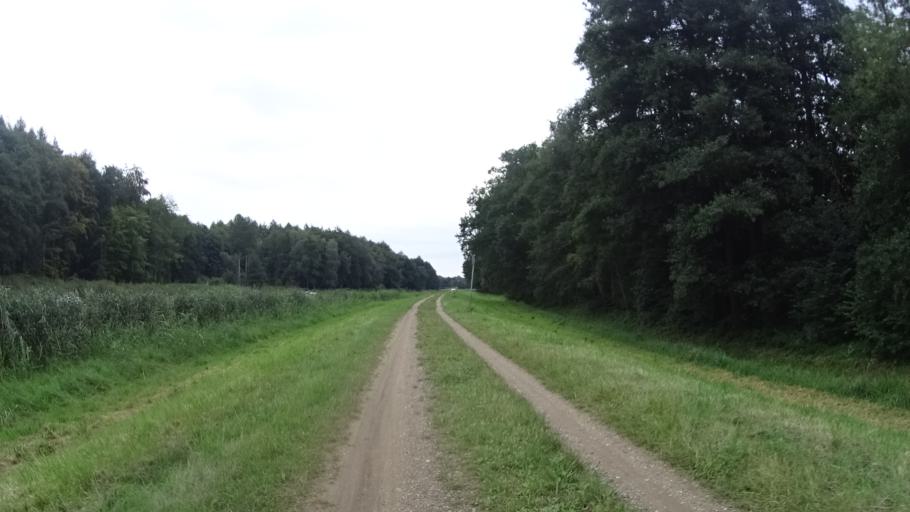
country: DE
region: Schleswig-Holstein
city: Lankau
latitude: 53.6510
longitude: 10.6464
